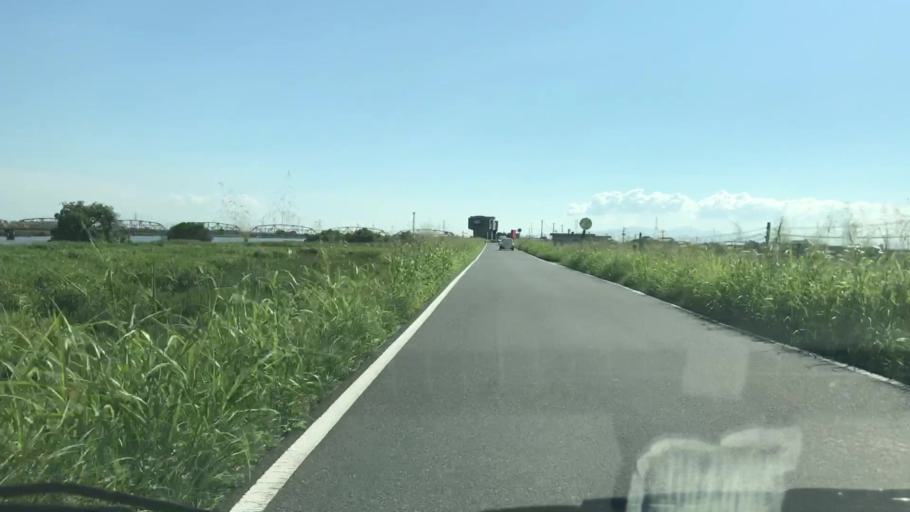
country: JP
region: Saga Prefecture
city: Kanzakimachi-kanzaki
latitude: 33.2661
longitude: 130.4203
